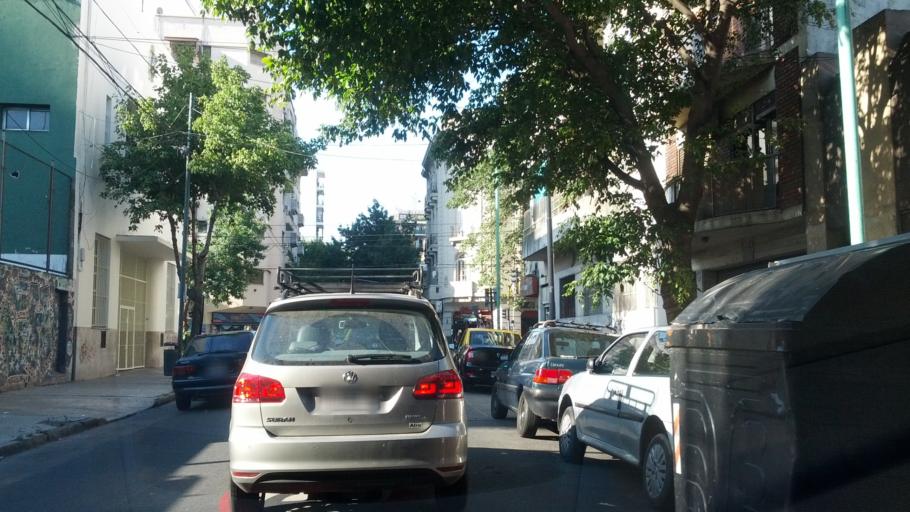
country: AR
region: Buenos Aires F.D.
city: Buenos Aires
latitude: -34.6230
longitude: -58.3872
